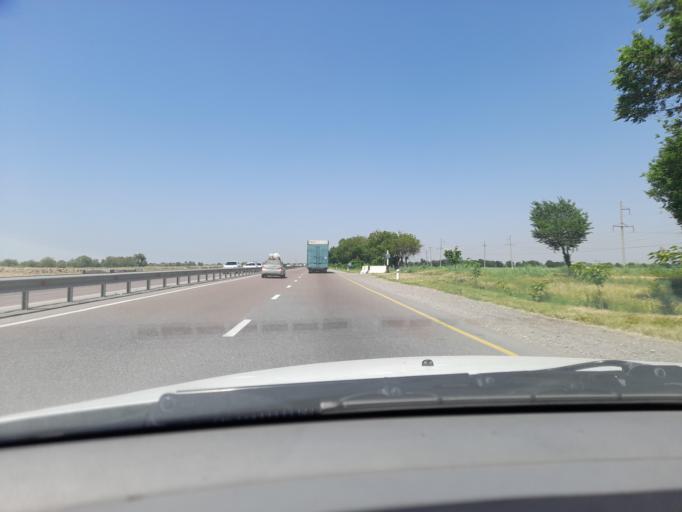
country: KZ
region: Ongtustik Qazaqstan
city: Myrzakent
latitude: 40.5297
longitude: 68.4406
